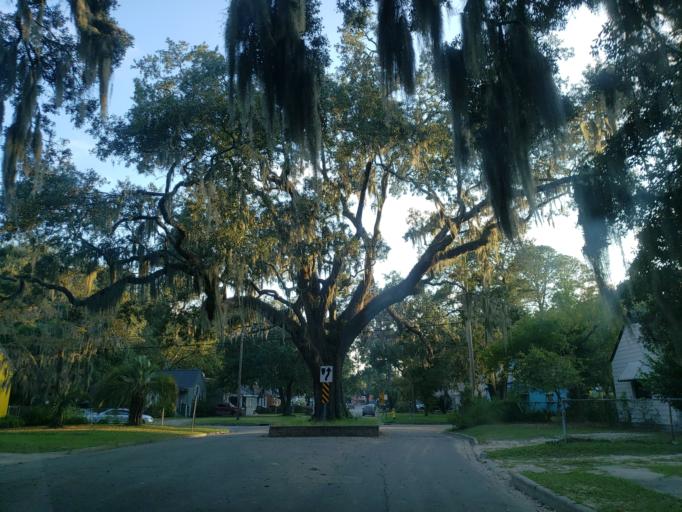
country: US
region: Georgia
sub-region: Chatham County
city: Thunderbolt
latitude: 32.0480
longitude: -81.0748
